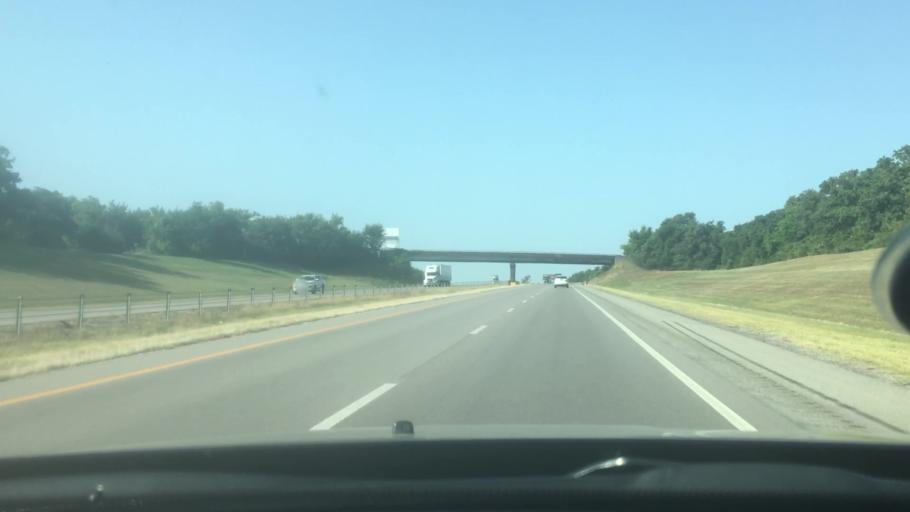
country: US
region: Oklahoma
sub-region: Bryan County
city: Durant
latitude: 33.9849
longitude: -96.4131
